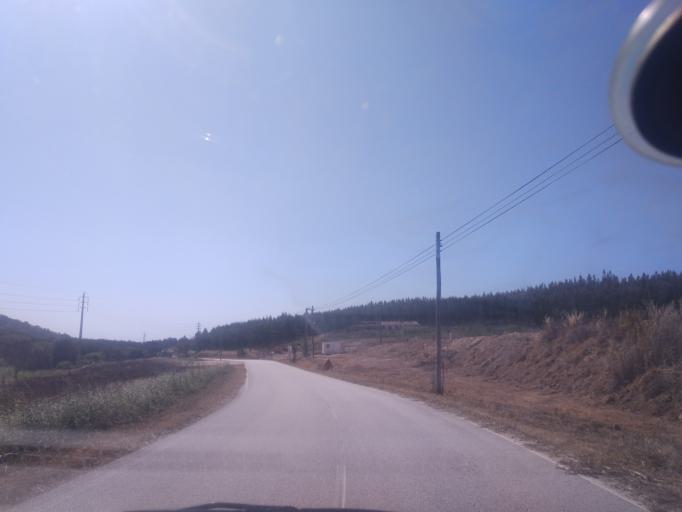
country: PT
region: Faro
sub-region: Aljezur
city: Aljezur
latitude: 37.2185
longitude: -8.7910
